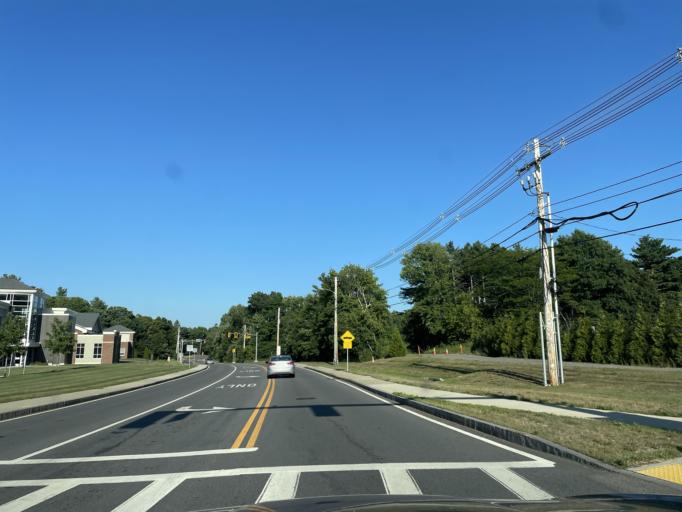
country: US
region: Massachusetts
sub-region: Bristol County
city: Mansfield
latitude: 42.0325
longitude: -71.1970
